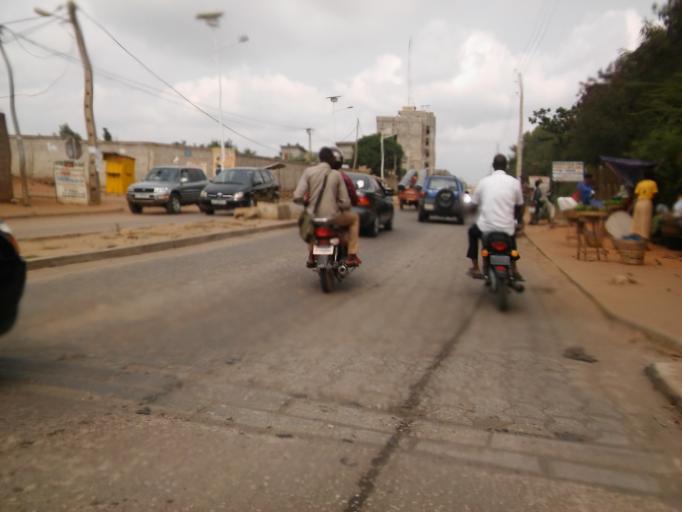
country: BJ
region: Atlantique
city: Abomey-Calavi
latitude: 6.4195
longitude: 2.3259
